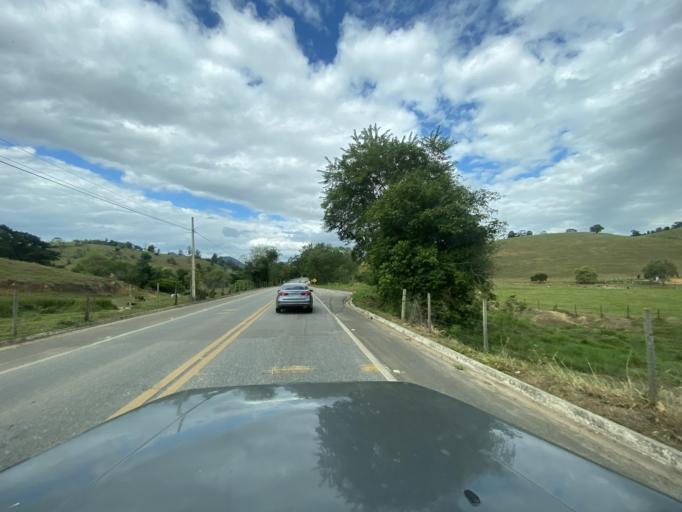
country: BR
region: Espirito Santo
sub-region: Jeronimo Monteiro
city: Jeronimo Monteiro
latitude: -20.7806
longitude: -41.4160
